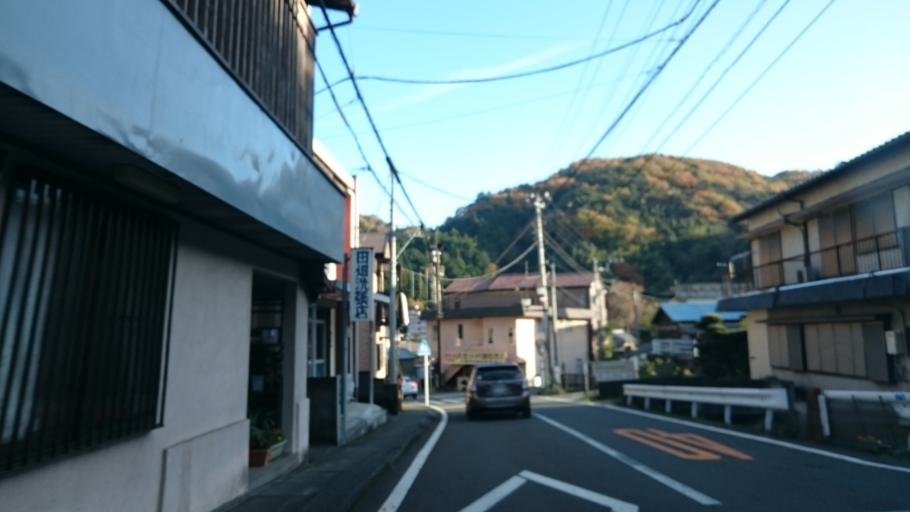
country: JP
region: Shizuoka
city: Numazu
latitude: 34.9726
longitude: 138.9293
